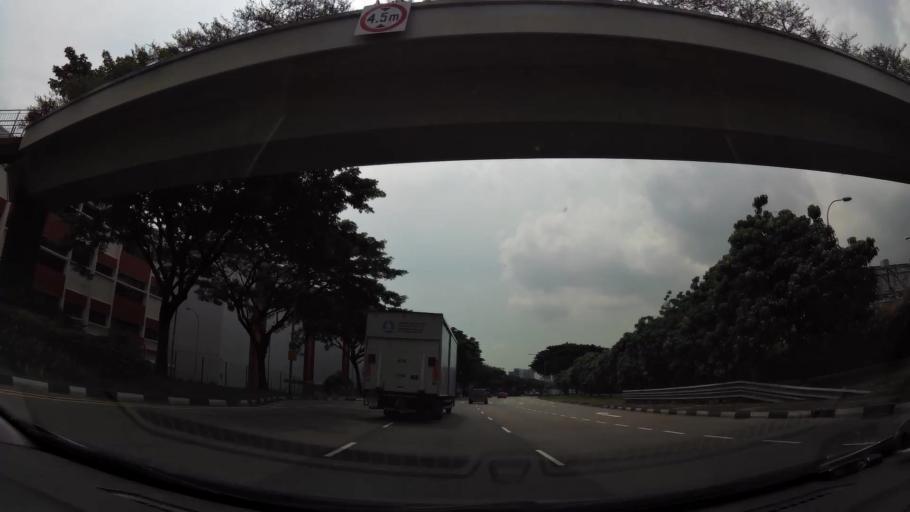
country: SG
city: Singapore
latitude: 1.3391
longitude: 103.8973
